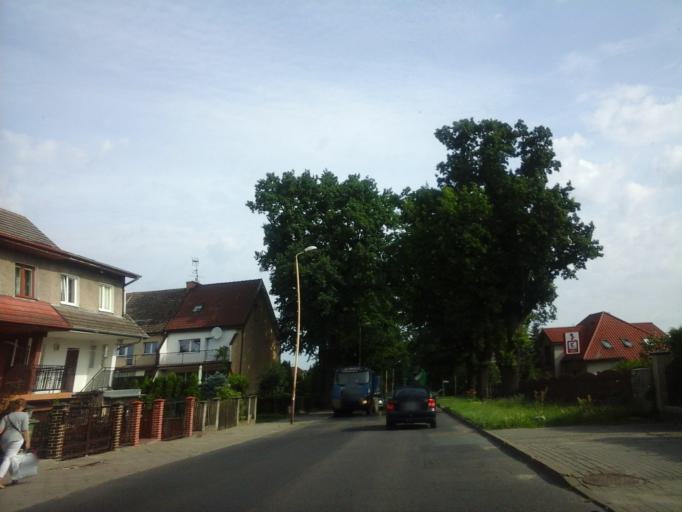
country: PL
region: West Pomeranian Voivodeship
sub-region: Powiat stargardzki
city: Stargard Szczecinski
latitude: 53.3241
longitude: 15.0399
